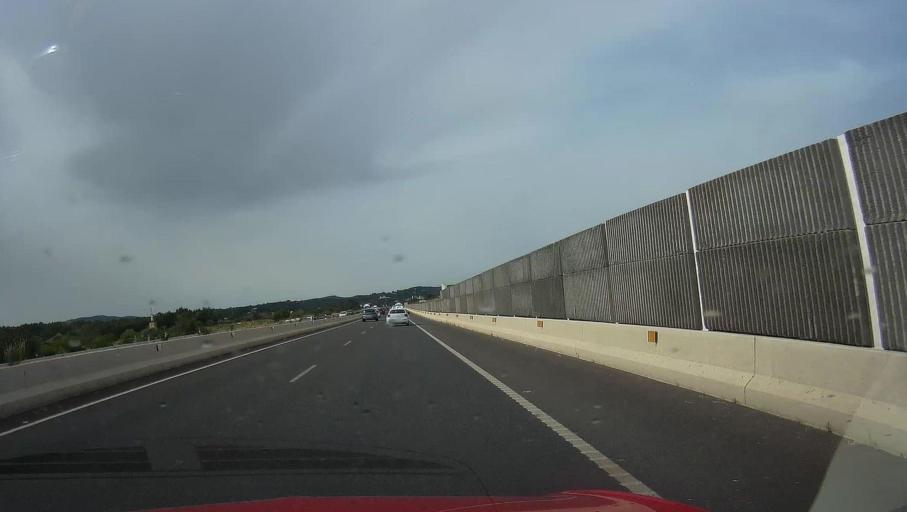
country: ES
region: Balearic Islands
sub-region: Illes Balears
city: Ibiza
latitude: 38.9464
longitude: 1.4435
